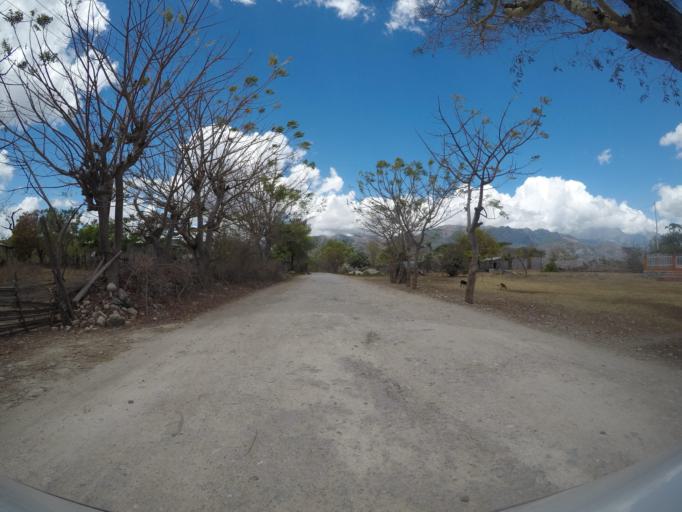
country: TL
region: Baucau
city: Baucau
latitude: -8.4844
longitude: 126.6144
